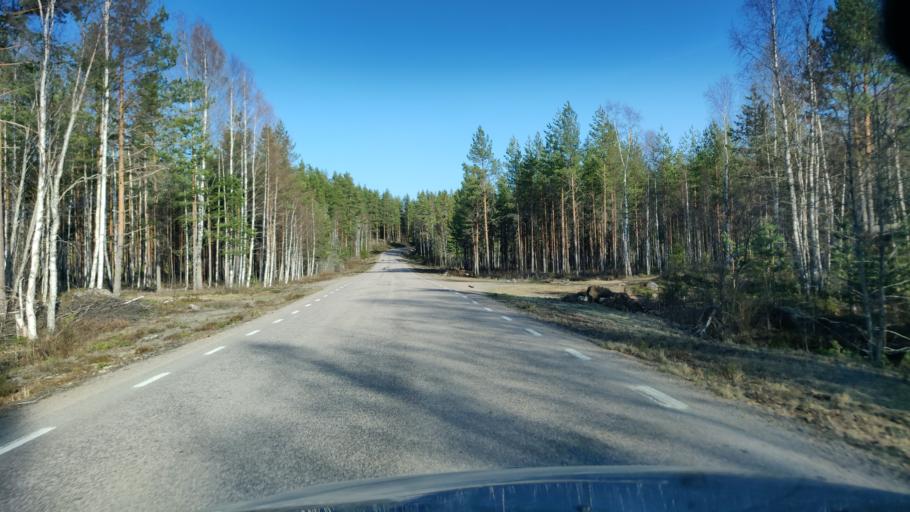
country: SE
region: Vaermland
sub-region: Hagfors Kommun
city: Ekshaerad
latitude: 59.9845
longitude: 13.3497
